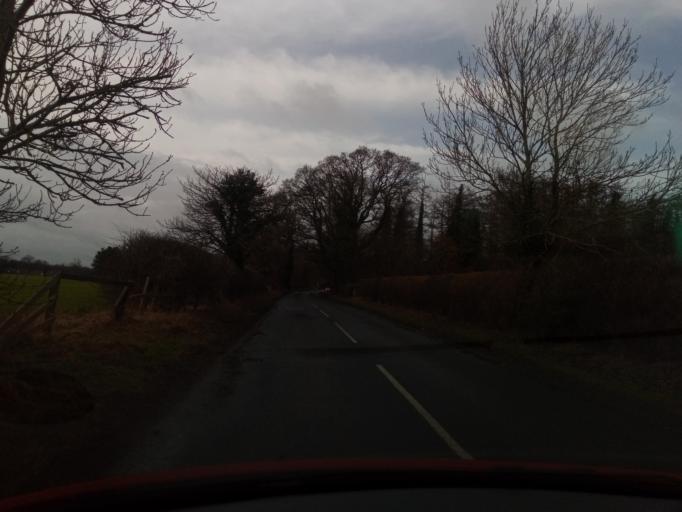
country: GB
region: England
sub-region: Northumberland
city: Corbridge
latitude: 54.9830
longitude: -2.0387
